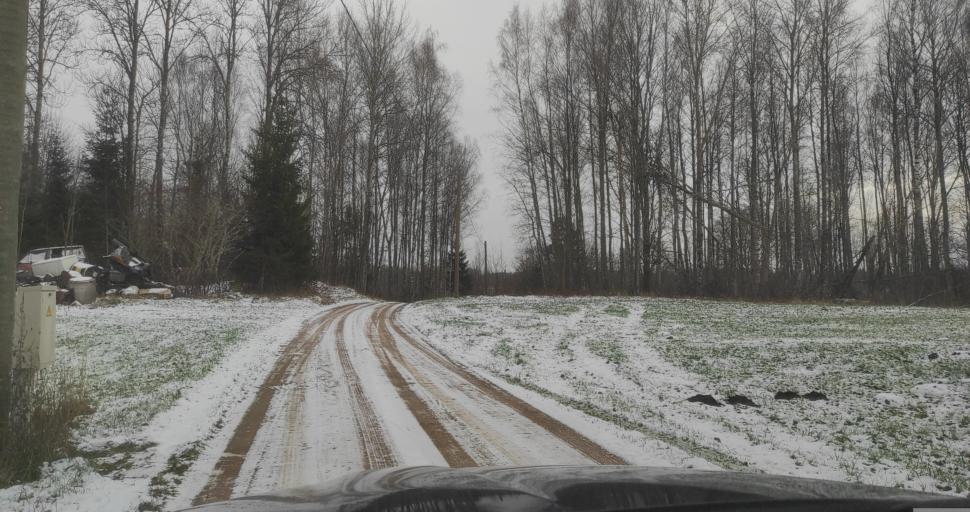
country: LV
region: Alsunga
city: Alsunga
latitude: 56.9599
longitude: 21.6419
